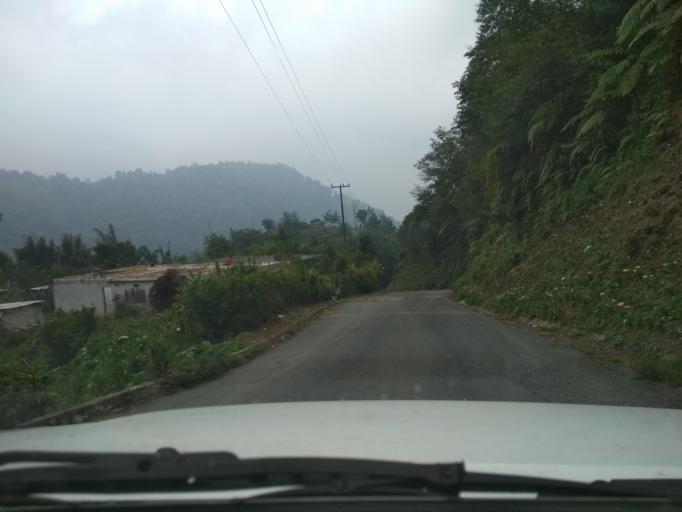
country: MX
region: Veracruz
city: La Perla
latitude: 18.9382
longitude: -97.1449
